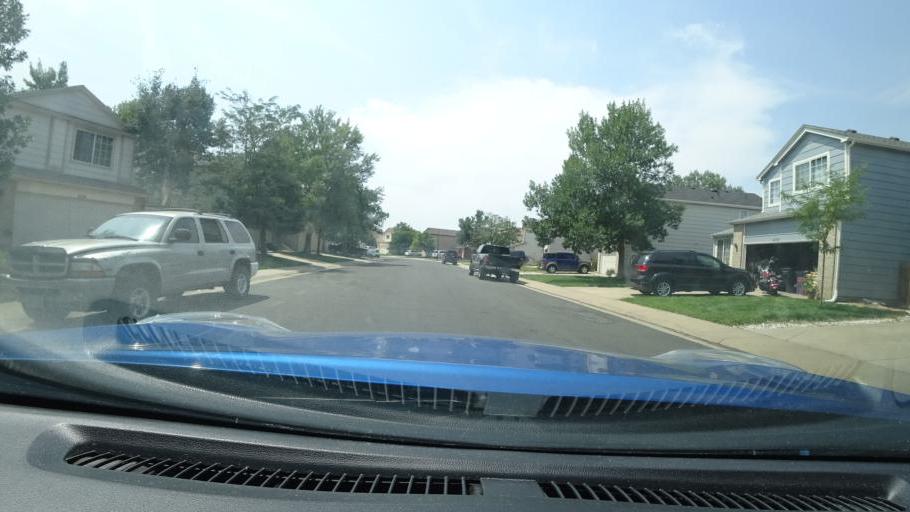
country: US
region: Colorado
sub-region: Adams County
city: Aurora
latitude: 39.7741
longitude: -104.7613
